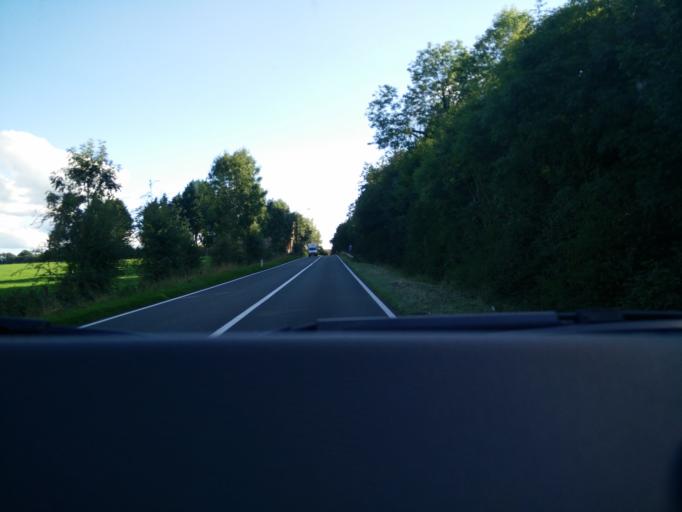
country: BE
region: Wallonia
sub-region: Province du Hainaut
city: Beaumont
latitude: 50.1887
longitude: 4.2193
